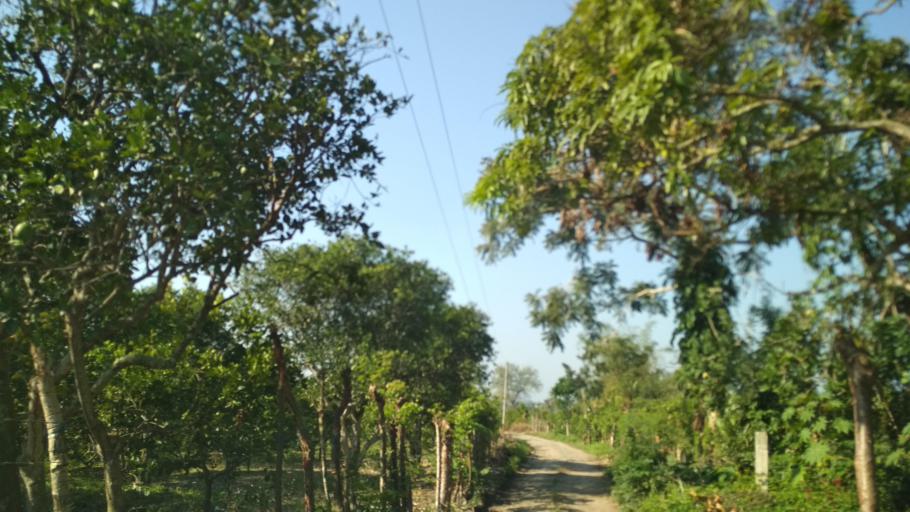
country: MX
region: Veracruz
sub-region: Papantla
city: Polutla
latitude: 20.4583
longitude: -97.2077
